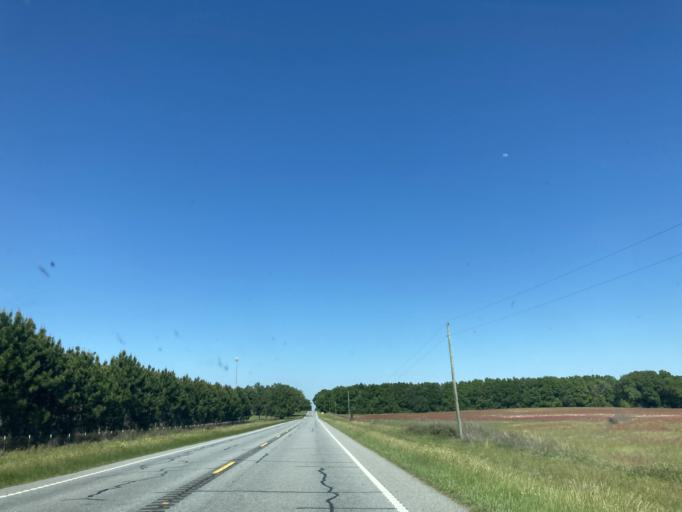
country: US
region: Georgia
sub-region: Baker County
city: Newton
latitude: 31.2665
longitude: -84.3982
